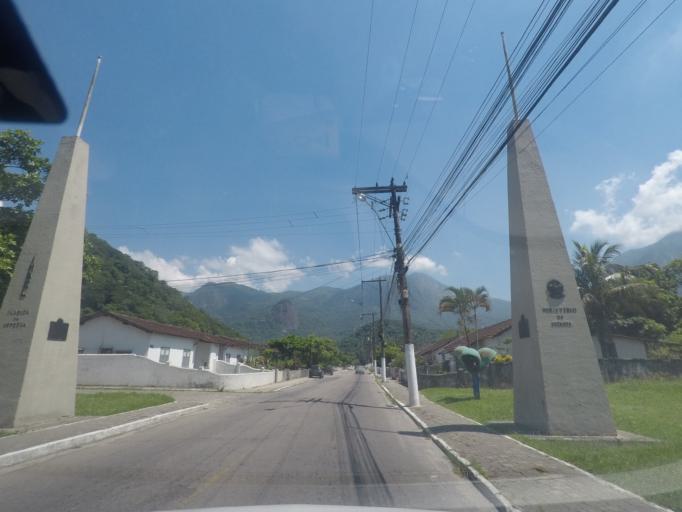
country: BR
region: Rio de Janeiro
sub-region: Petropolis
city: Petropolis
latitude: -22.5819
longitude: -43.1870
